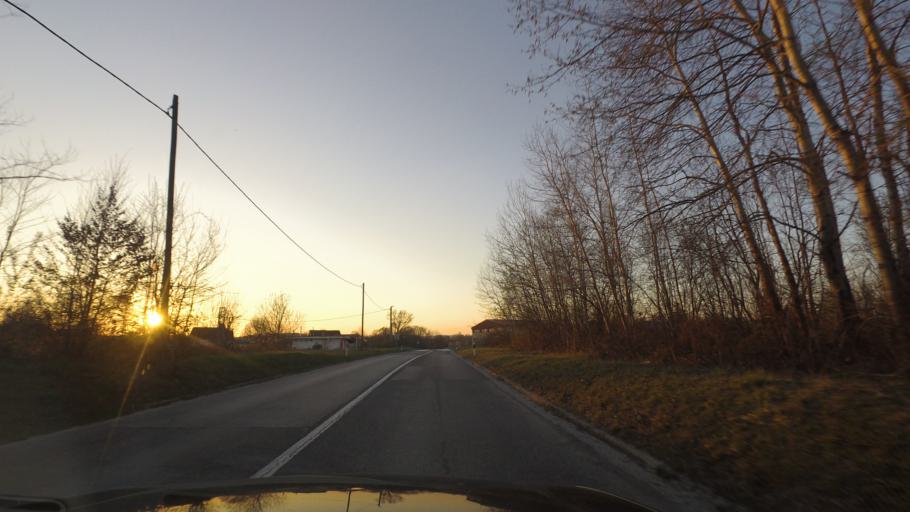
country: HR
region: Sisacko-Moslavacka
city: Gvozd
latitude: 45.3379
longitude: 15.9014
